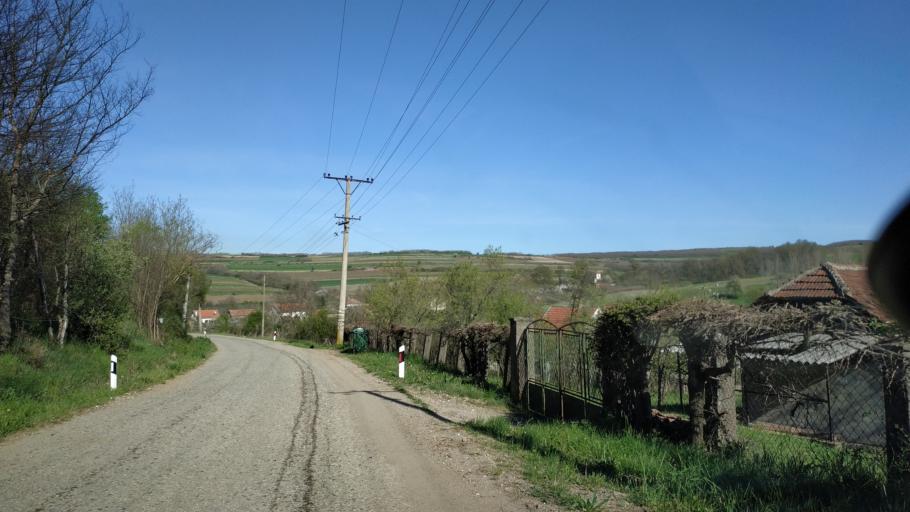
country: RS
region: Central Serbia
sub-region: Nisavski Okrug
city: Aleksinac
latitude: 43.4760
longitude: 21.6485
